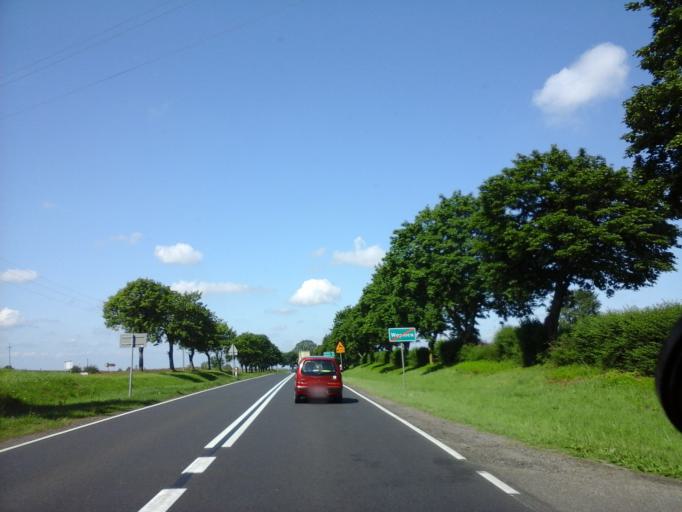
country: PL
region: West Pomeranian Voivodeship
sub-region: Powiat stargardzki
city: Dobrzany
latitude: 53.2728
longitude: 15.4559
